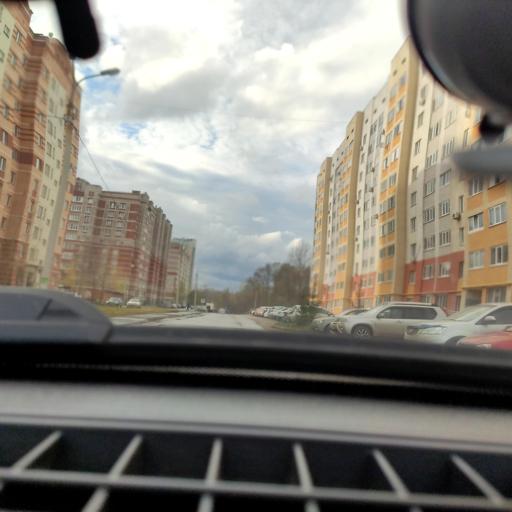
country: RU
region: Bashkortostan
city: Ufa
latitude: 54.7848
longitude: 56.1148
